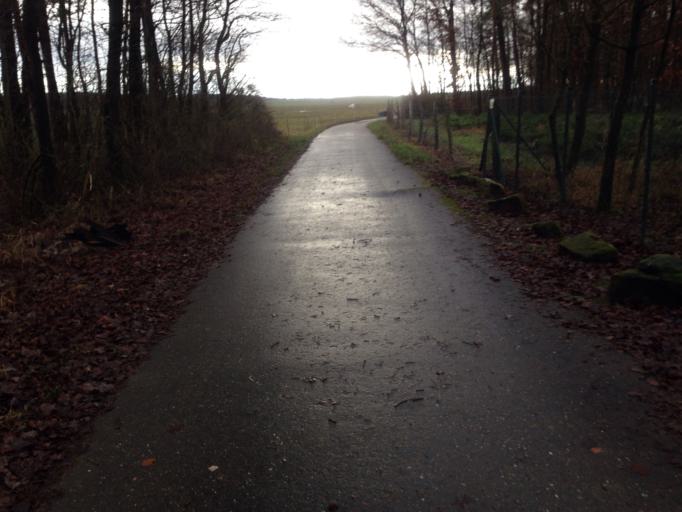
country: DE
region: Baden-Wuerttemberg
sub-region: Karlsruhe Region
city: Limbach
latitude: 49.4073
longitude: 9.2276
